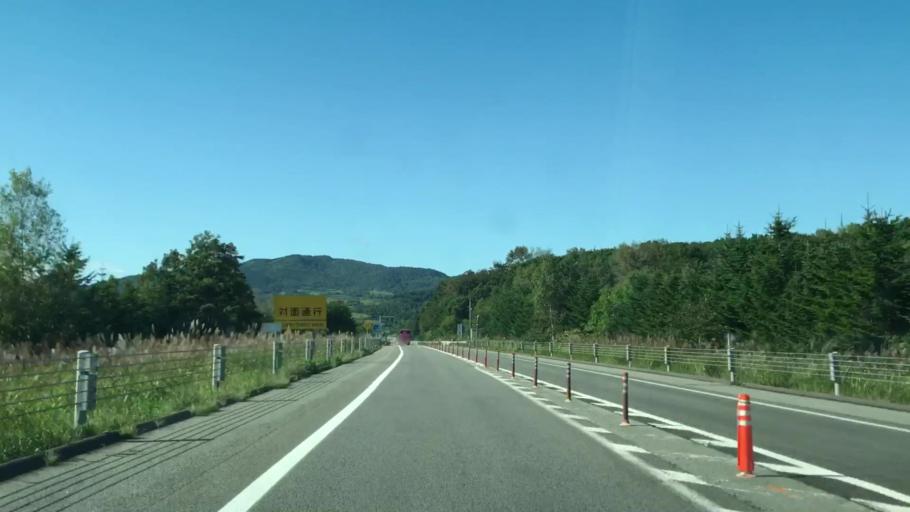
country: JP
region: Hokkaido
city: Date
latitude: 42.5339
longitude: 140.7986
